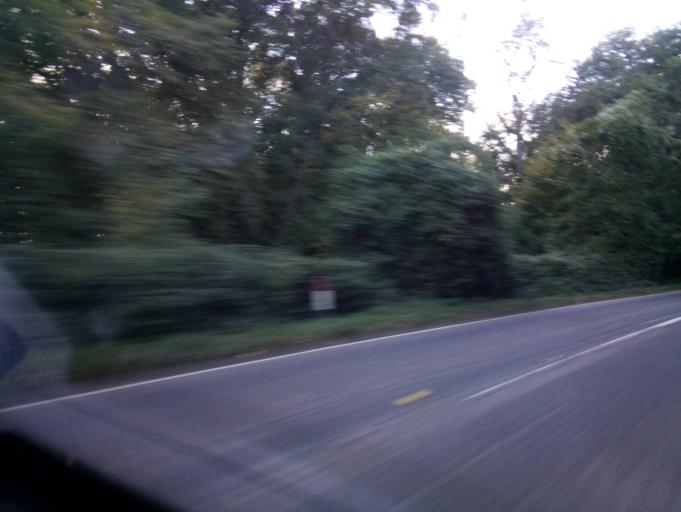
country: GB
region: England
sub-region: Herefordshire
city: Donnington
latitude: 52.0222
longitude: -2.3311
